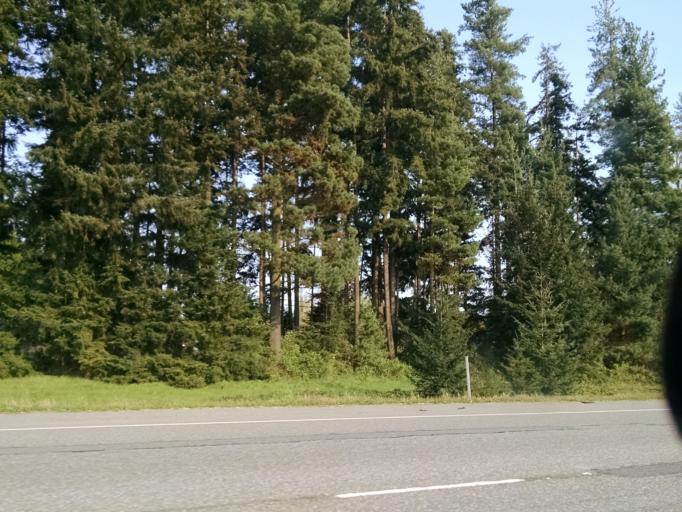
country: US
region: Washington
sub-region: Snohomish County
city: Marysville
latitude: 48.0808
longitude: -122.1847
